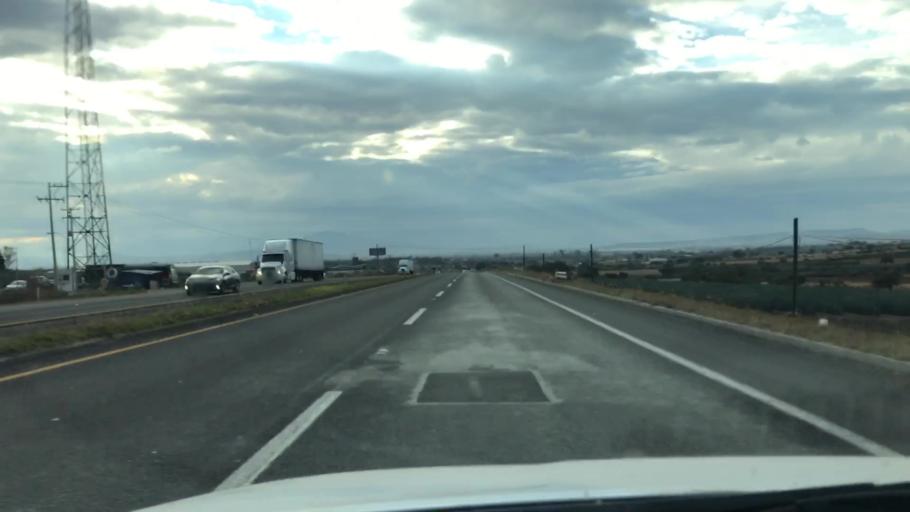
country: MX
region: Guanajuato
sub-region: Penjamo
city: Mezquite de Luna
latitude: 20.3786
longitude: -101.8423
